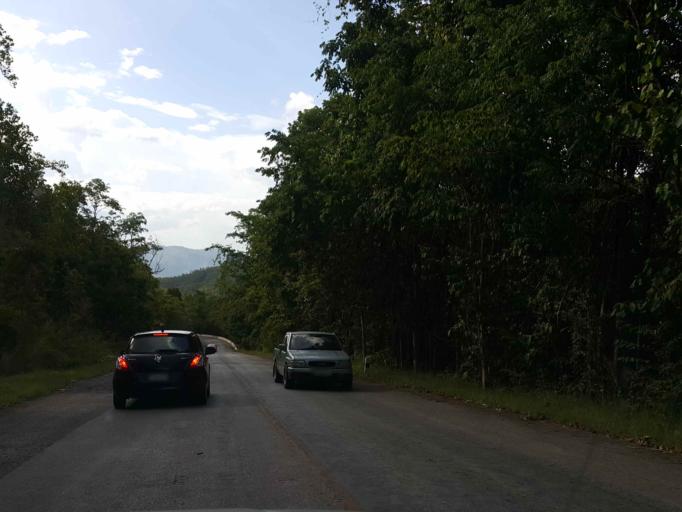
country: TH
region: Lampang
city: Thoen
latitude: 17.6239
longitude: 99.3134
